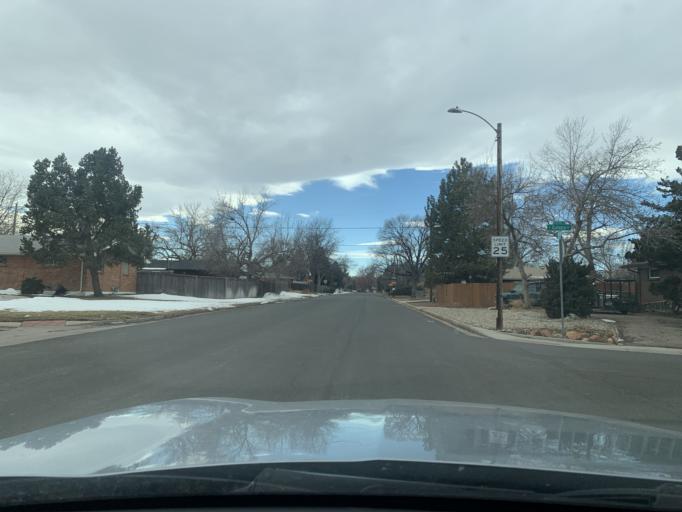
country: US
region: Colorado
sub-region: Arapahoe County
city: Glendale
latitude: 39.6590
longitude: -104.8703
